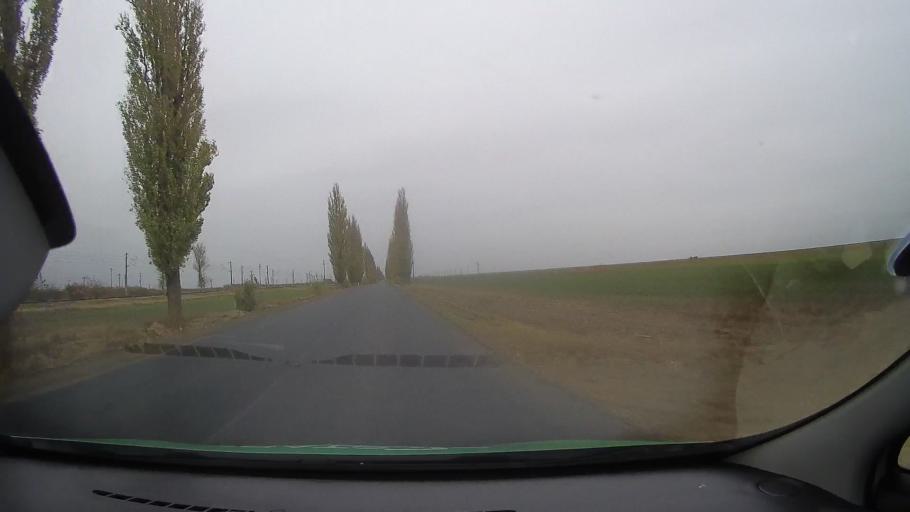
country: RO
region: Ialomita
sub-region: Comuna Valea Ciorii
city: Valea Ciorii
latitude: 44.7114
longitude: 27.5919
